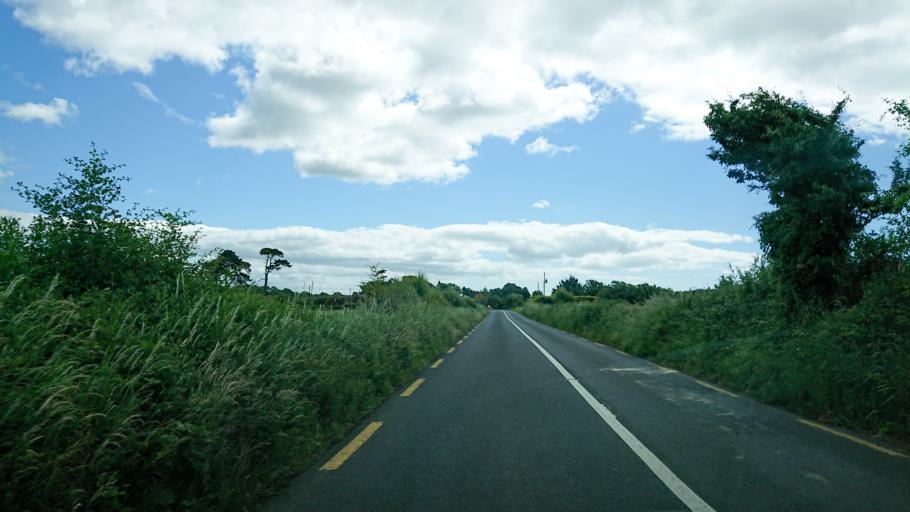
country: IE
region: Munster
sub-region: Waterford
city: Tra Mhor
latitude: 52.1791
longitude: -7.1626
